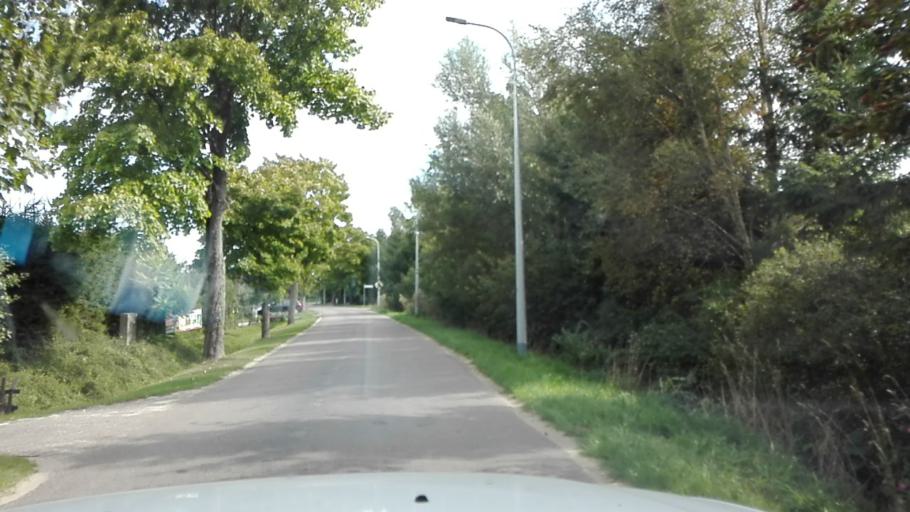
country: PL
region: West Pomeranian Voivodeship
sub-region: Powiat slawienski
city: Slawno
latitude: 54.5311
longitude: 16.5861
